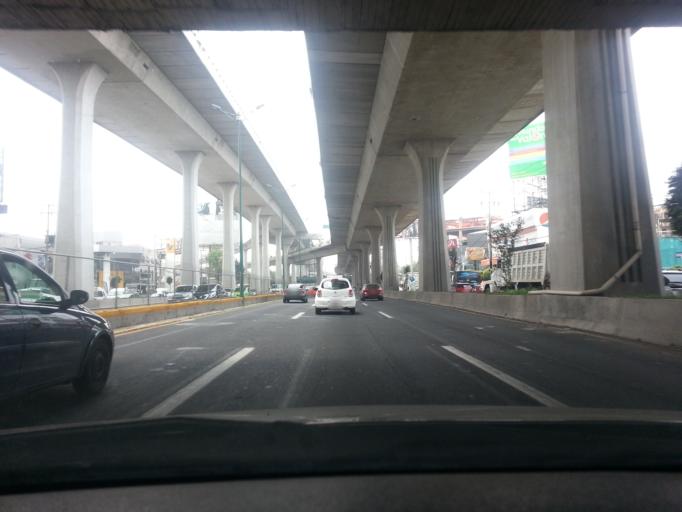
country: MX
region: Mexico
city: Naucalpan de Juarez
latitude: 19.4848
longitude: -99.2346
